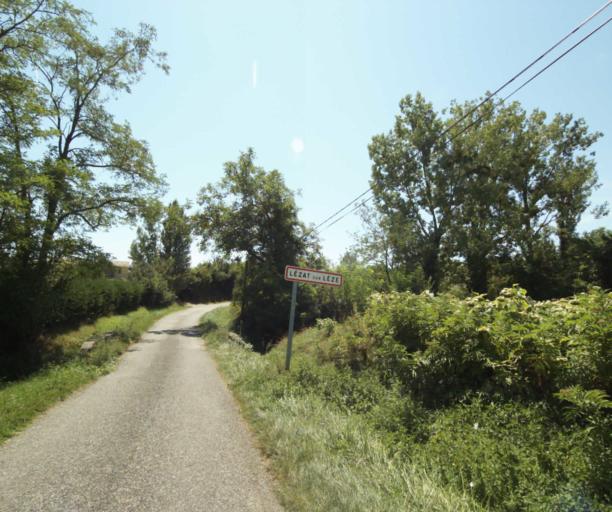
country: FR
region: Midi-Pyrenees
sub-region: Departement de l'Ariege
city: Lezat-sur-Leze
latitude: 43.2829
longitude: 1.3438
